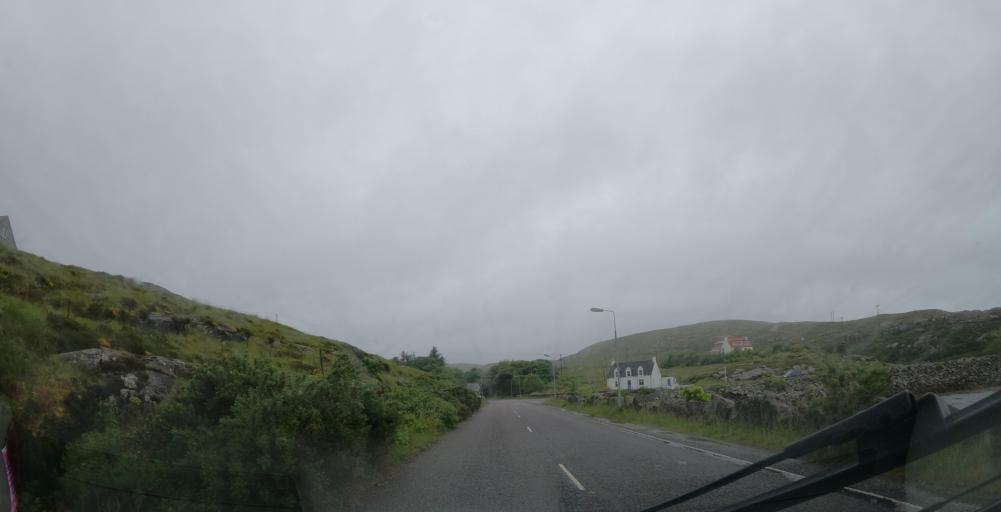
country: GB
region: Scotland
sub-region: Eilean Siar
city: Barra
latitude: 57.0016
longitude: -7.4293
